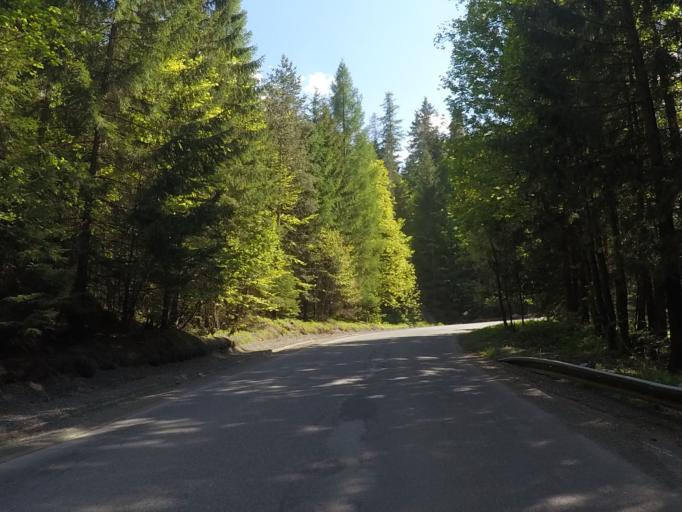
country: SK
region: Kosicky
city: Dobsina
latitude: 48.9123
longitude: 20.2605
